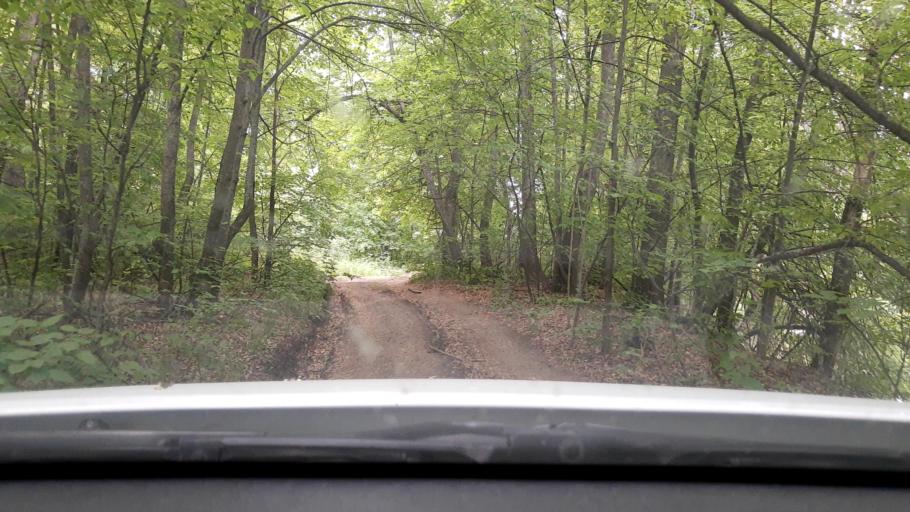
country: RU
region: Bashkortostan
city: Ufa
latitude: 54.6570
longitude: 55.8804
